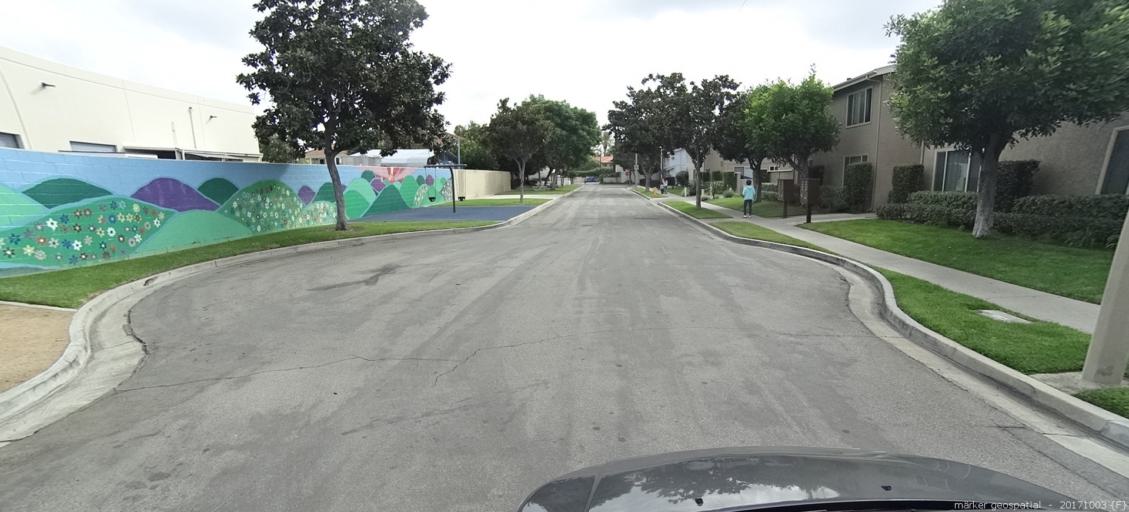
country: US
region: California
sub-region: Orange County
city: Garden Grove
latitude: 33.7585
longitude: -117.9091
